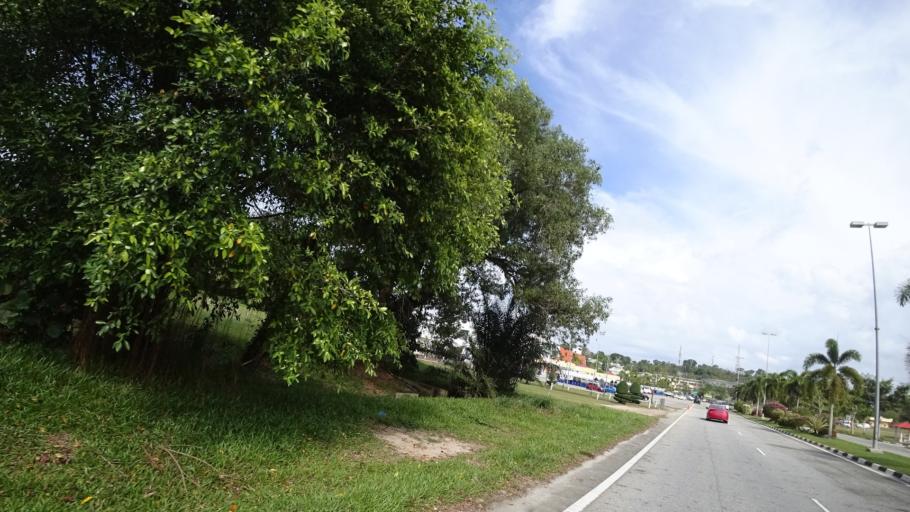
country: BN
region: Tutong
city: Tutong
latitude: 4.8149
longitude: 114.6606
